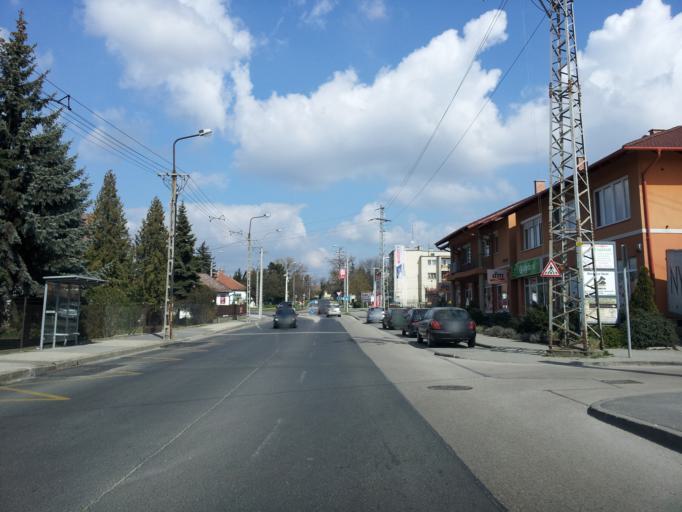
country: HU
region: Pest
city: Erd
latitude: 47.3857
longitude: 18.9248
